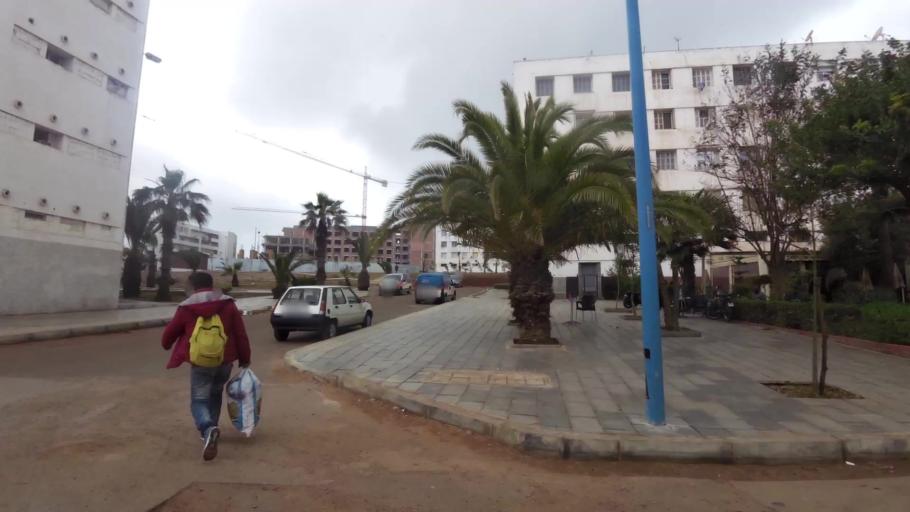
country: MA
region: Grand Casablanca
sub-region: Casablanca
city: Casablanca
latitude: 33.6043
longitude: -7.6526
